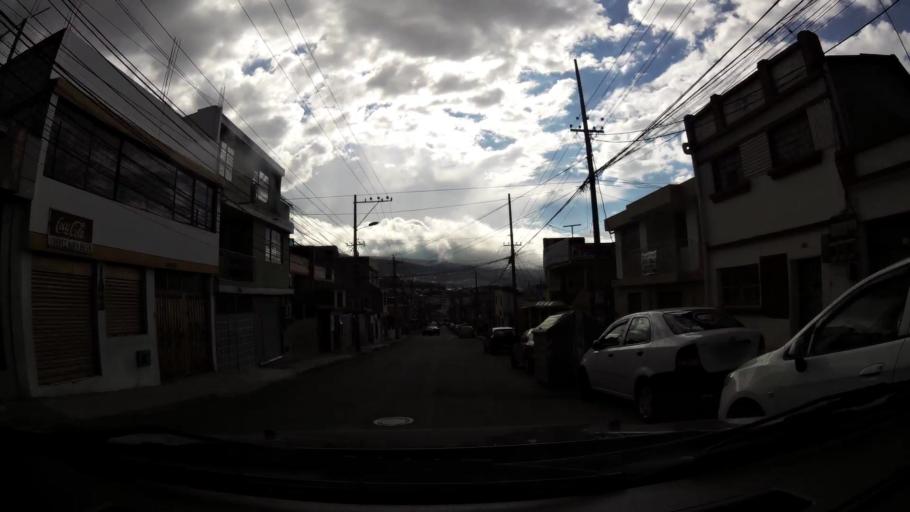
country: EC
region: Pichincha
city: Quito
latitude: -0.1164
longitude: -78.4877
